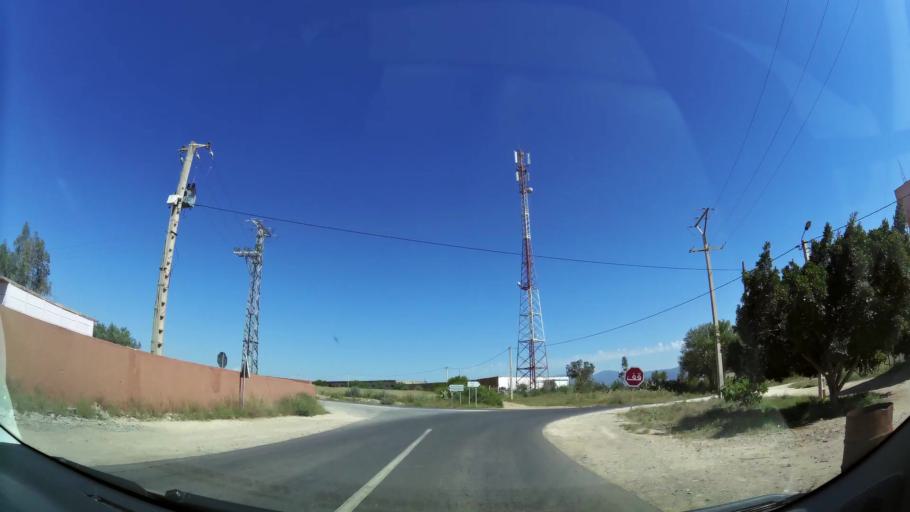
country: MA
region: Oriental
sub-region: Berkane-Taourirt
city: Madagh
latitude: 35.0121
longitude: -2.3976
